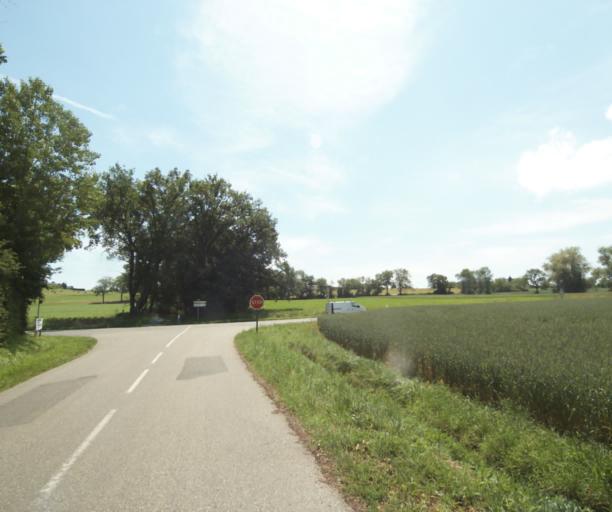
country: FR
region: Rhone-Alpes
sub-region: Departement de la Haute-Savoie
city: Messery
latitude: 46.3576
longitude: 6.3062
